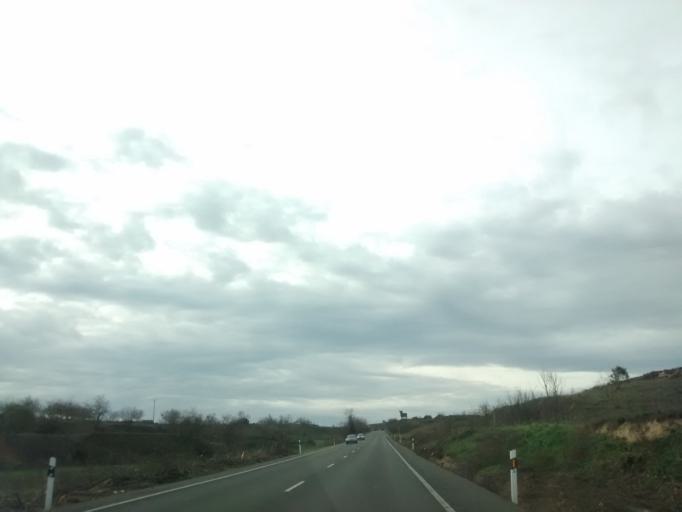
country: ES
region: La Rioja
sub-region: Provincia de La Rioja
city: Torremontalbo
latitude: 42.5094
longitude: -2.7117
